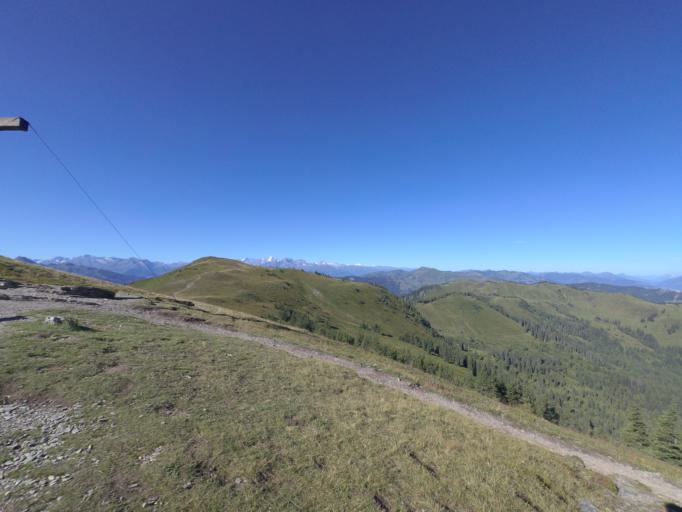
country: AT
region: Salzburg
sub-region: Politischer Bezirk Sankt Johann im Pongau
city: Goldegg
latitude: 47.3694
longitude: 13.0734
